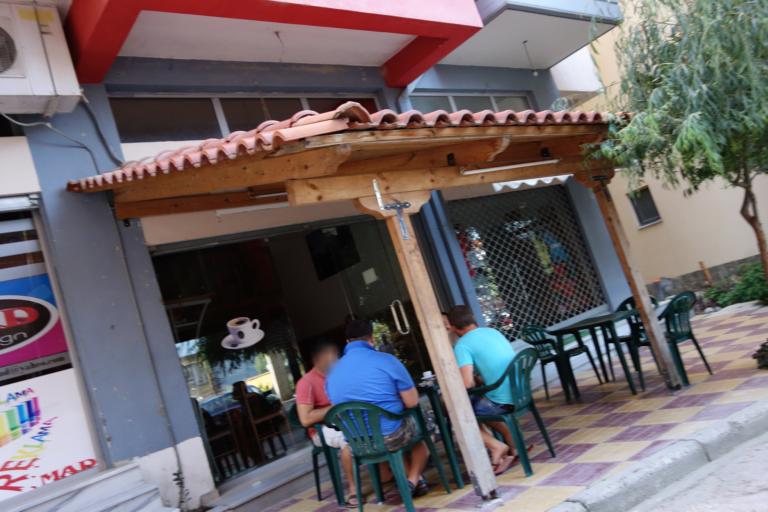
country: AL
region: Gjirokaster
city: Gjirokaster
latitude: 40.0797
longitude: 20.1483
